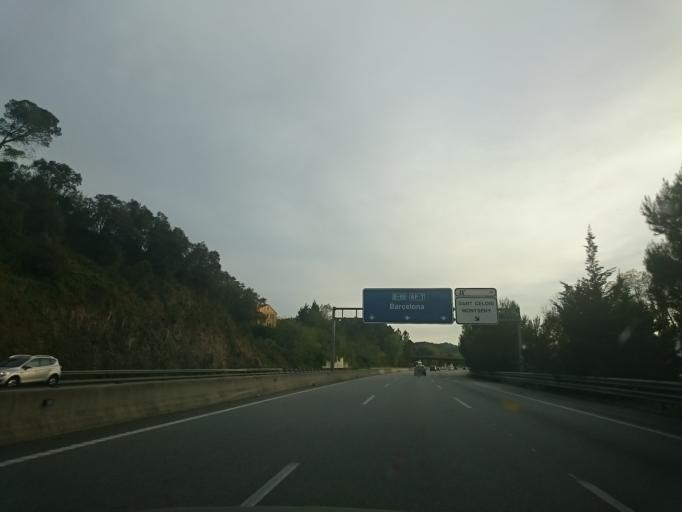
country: ES
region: Catalonia
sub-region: Provincia de Barcelona
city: Sant Celoni
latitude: 41.6764
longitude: 2.4866
